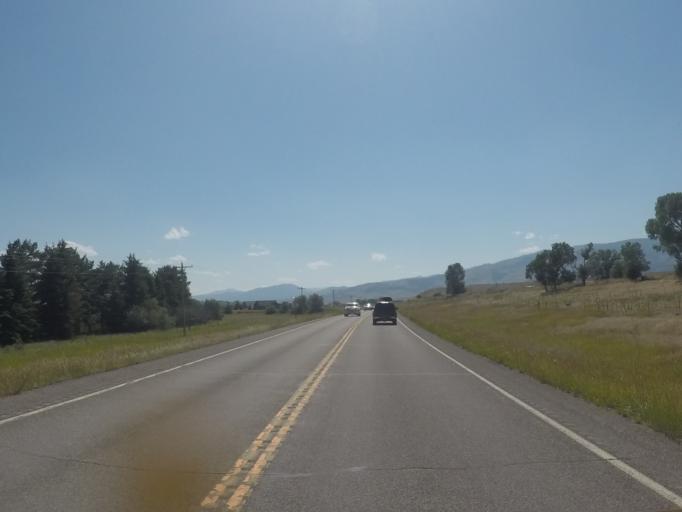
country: US
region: Montana
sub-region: Park County
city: Livingston
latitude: 45.4257
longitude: -110.6483
